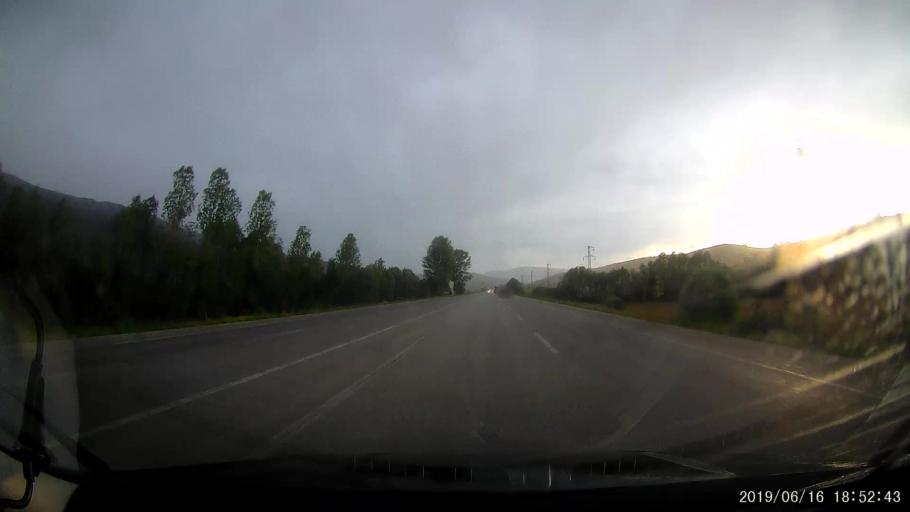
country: TR
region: Erzincan
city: Catalcam
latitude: 39.9014
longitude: 38.8947
